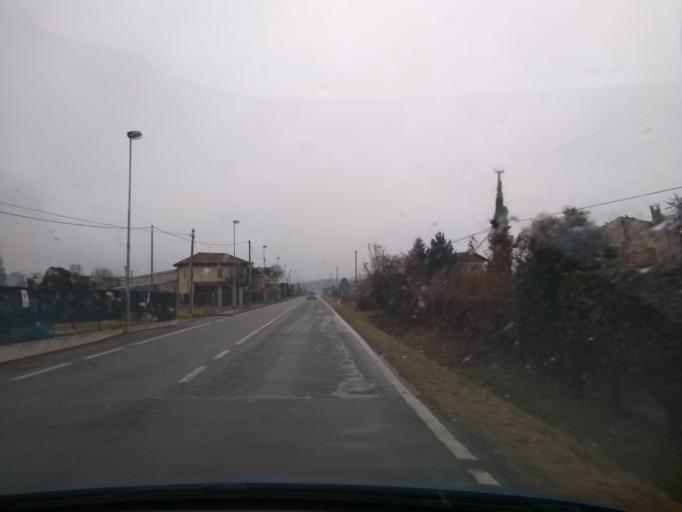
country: IT
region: Piedmont
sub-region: Provincia di Torino
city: Valperga
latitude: 45.3755
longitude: 7.6583
